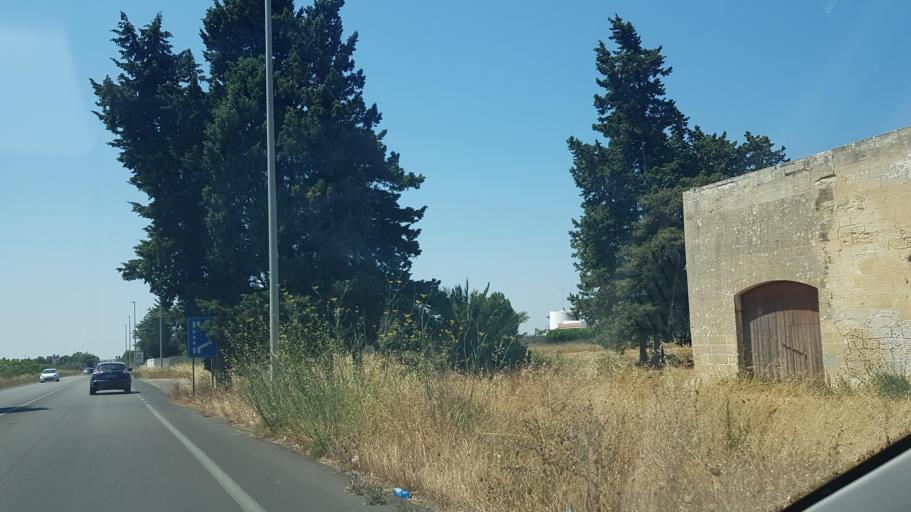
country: IT
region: Apulia
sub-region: Provincia di Lecce
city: Merine
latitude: 40.3386
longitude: 18.2265
